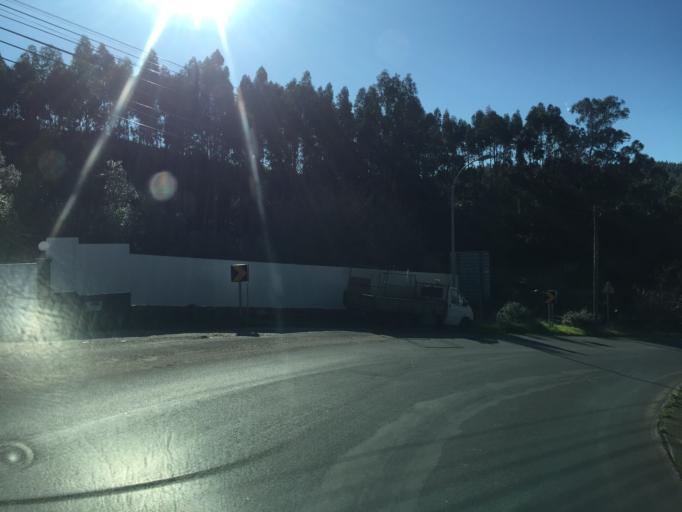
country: PT
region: Lisbon
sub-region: Sintra
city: Almargem
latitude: 38.8140
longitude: -9.2918
